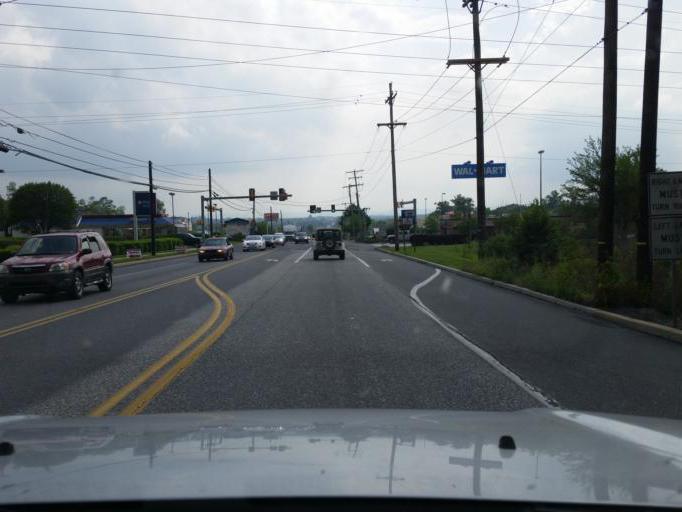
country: US
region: Pennsylvania
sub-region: Adams County
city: Gettysburg
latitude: 39.8441
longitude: -77.2011
